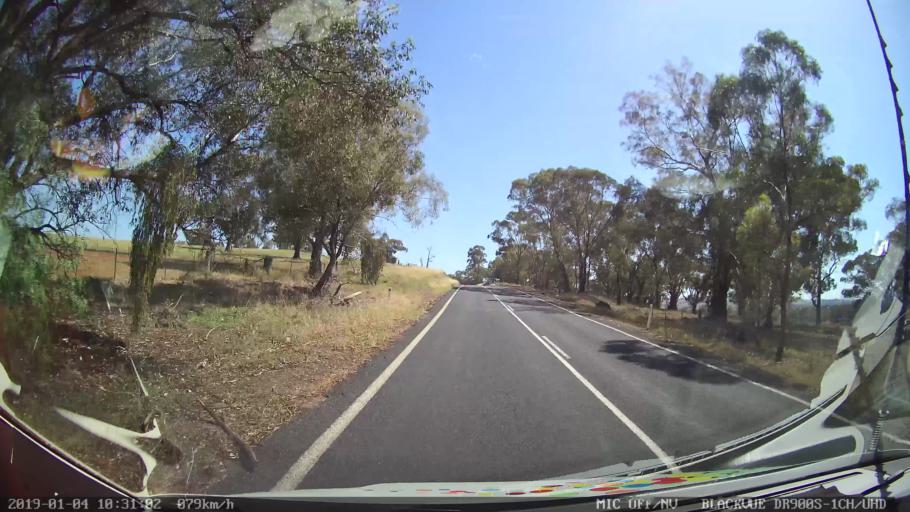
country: AU
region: New South Wales
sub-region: Cabonne
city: Canowindra
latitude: -33.3394
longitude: 148.6309
